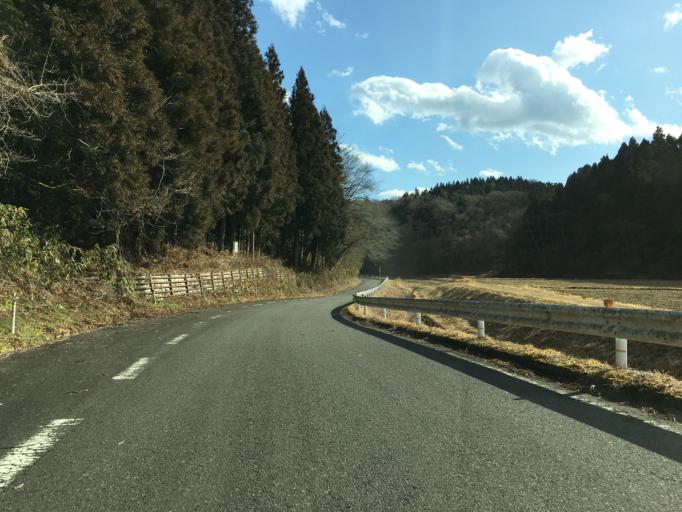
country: JP
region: Fukushima
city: Ishikawa
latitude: 37.2281
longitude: 140.5944
